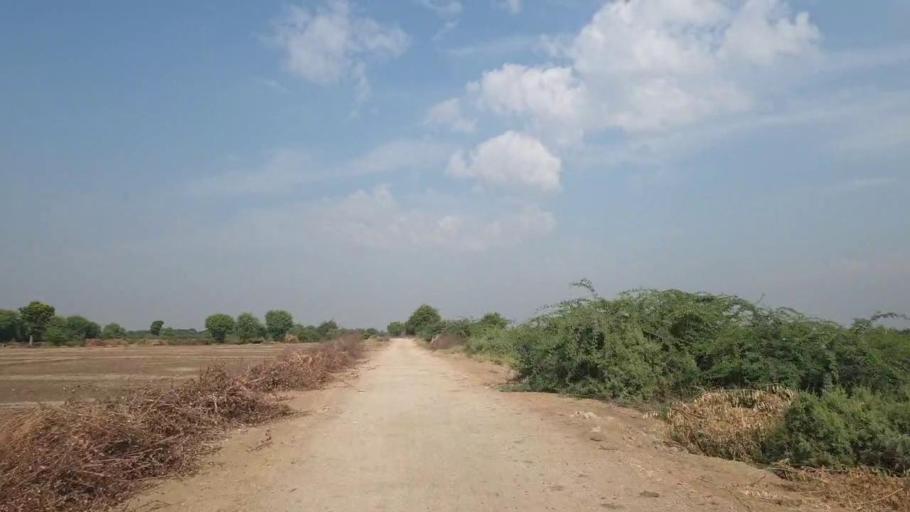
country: PK
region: Sindh
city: Digri
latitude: 25.0130
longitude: 69.0660
